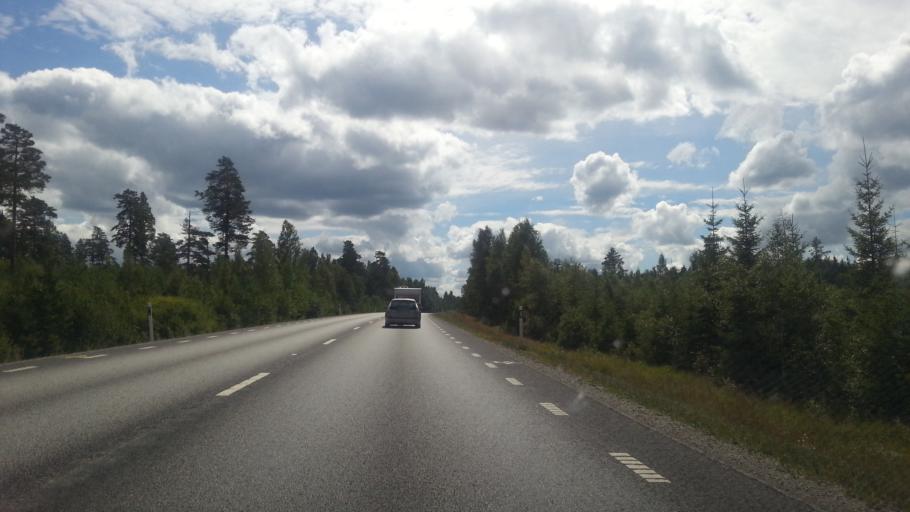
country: SE
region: OErebro
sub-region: Lindesbergs Kommun
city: Lindesberg
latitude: 59.5645
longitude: 15.2168
